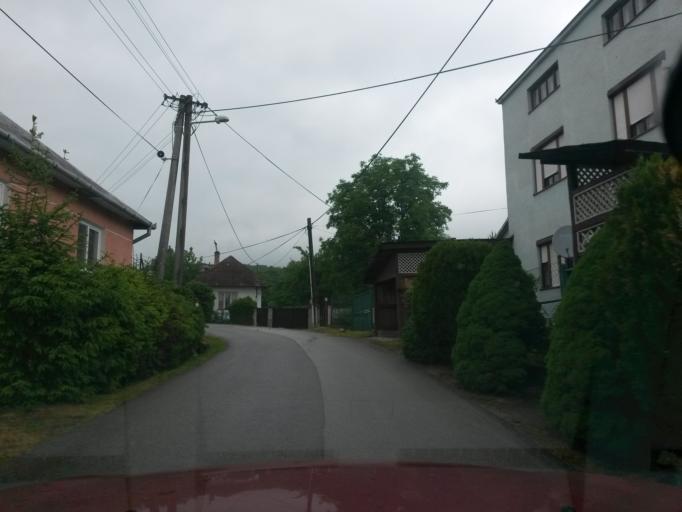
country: SK
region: Kosicky
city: Moldava nad Bodvou
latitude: 48.6914
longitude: 21.0717
